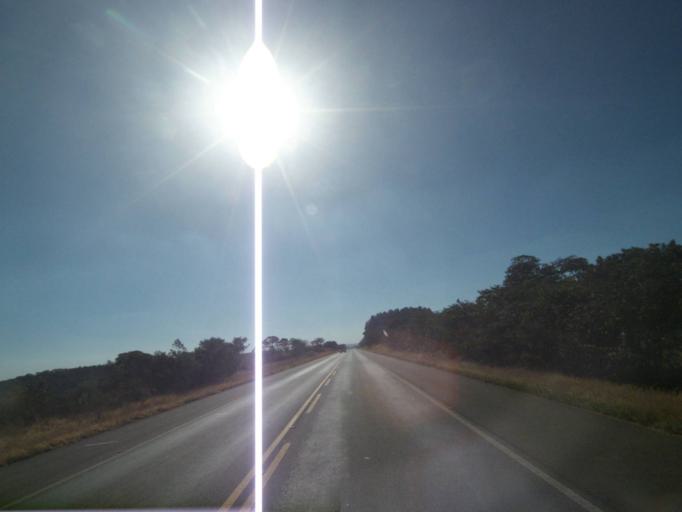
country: BR
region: Parana
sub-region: Tibagi
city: Tibagi
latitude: -24.7671
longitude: -50.4682
